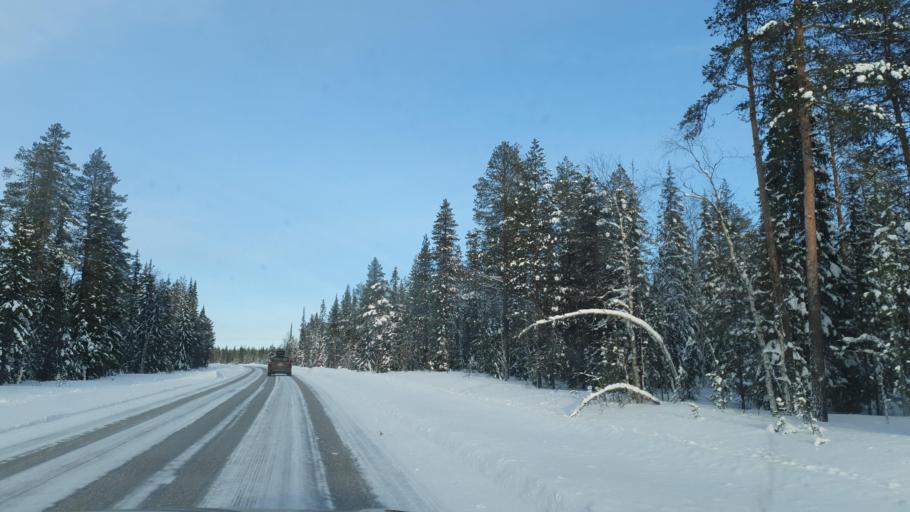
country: FI
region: Lapland
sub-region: Tunturi-Lappi
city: Kolari
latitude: 67.4943
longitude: 23.8966
